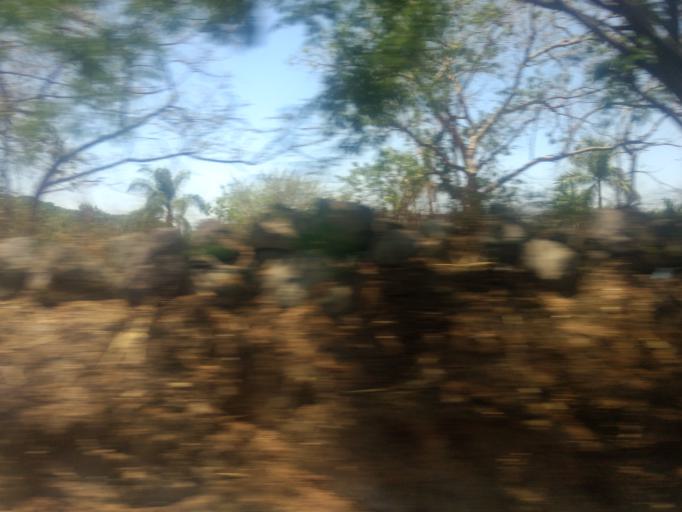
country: MX
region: Colima
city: Cuauhtemoc
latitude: 19.2950
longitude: -103.6463
